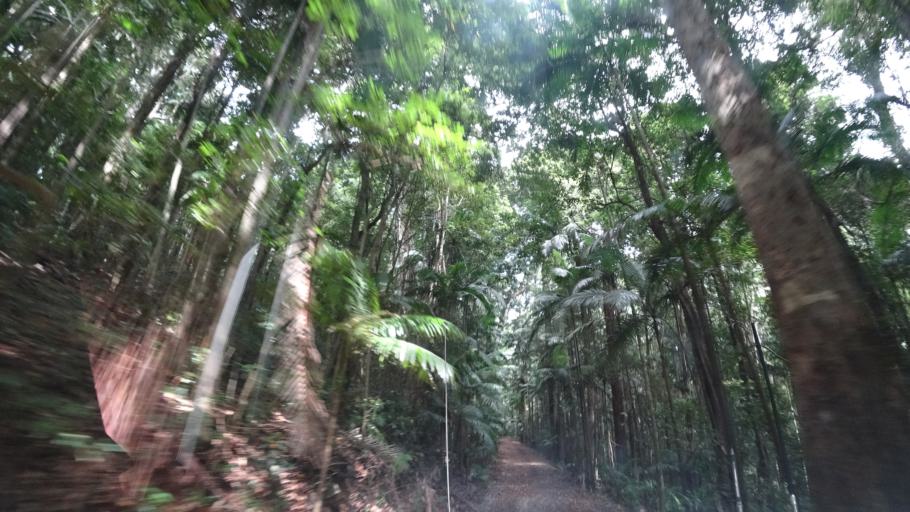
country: AU
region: Queensland
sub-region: Moreton Bay
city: Highvale
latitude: -27.3324
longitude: 152.7614
